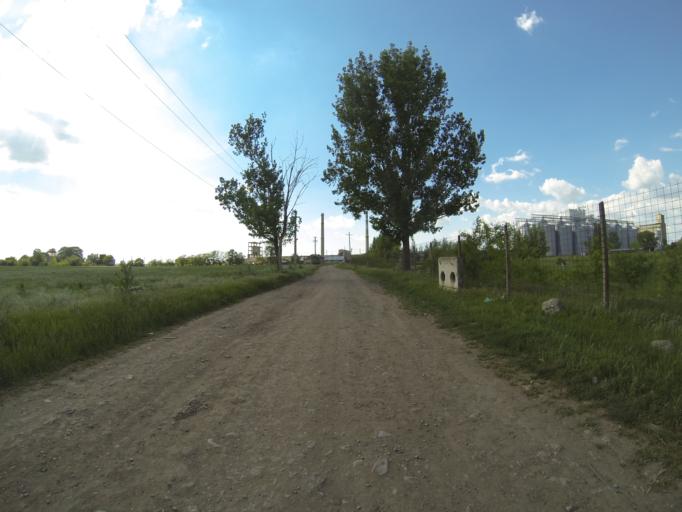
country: RO
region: Dolj
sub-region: Comuna Segarcea
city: Segarcea
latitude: 44.0819
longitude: 23.7293
